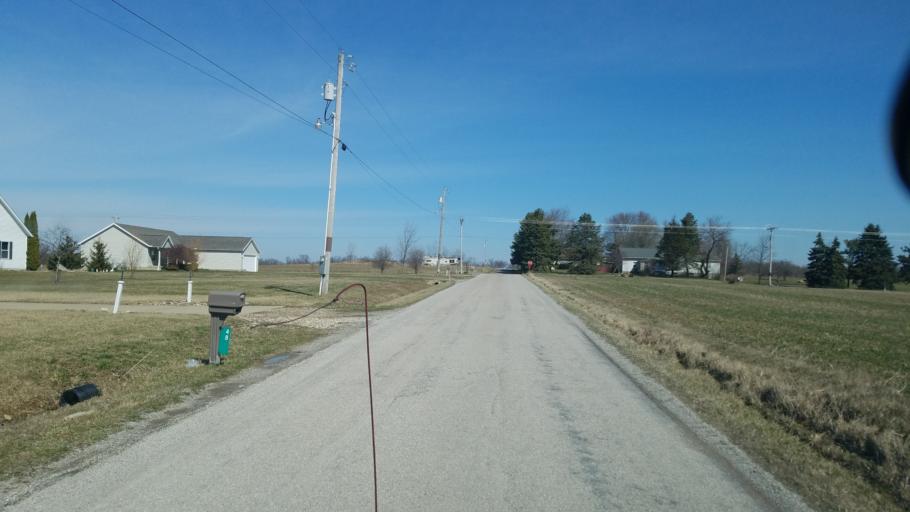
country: US
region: Ohio
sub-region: Lorain County
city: Wellington
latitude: 41.0566
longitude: -82.2399
